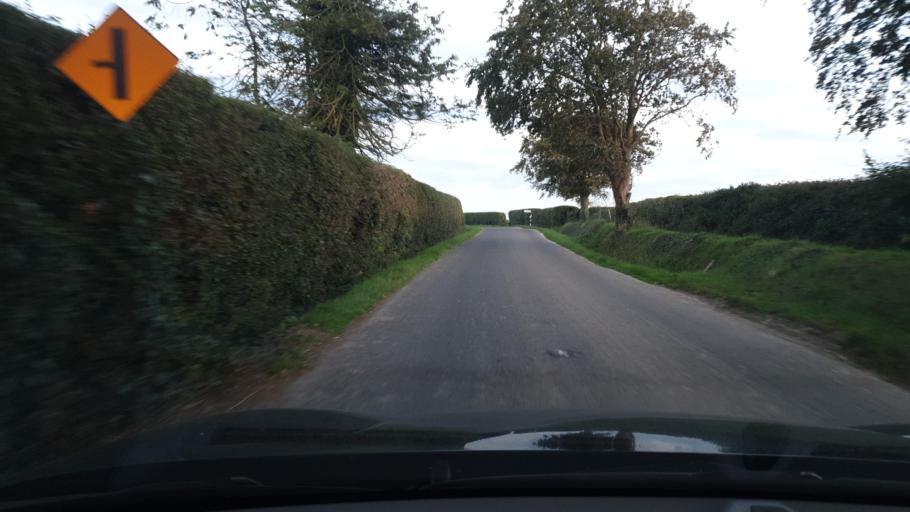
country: IE
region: Leinster
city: Lusk
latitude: 53.5578
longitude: -6.1684
